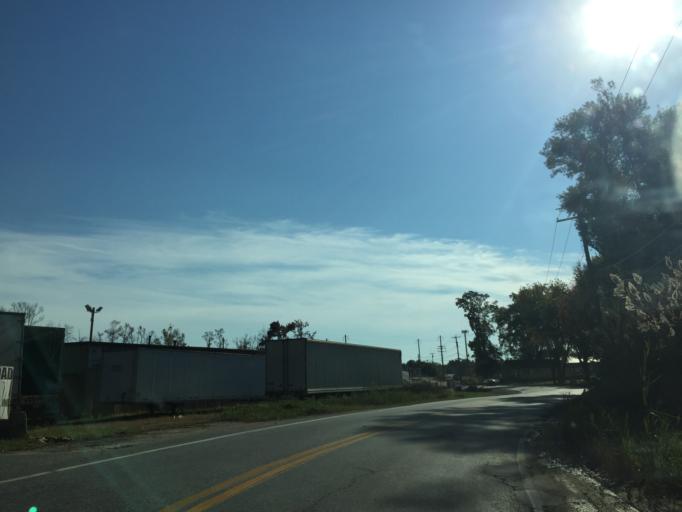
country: US
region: Maryland
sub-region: Baltimore County
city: Bowleys Quarters
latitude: 39.3493
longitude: -76.3937
